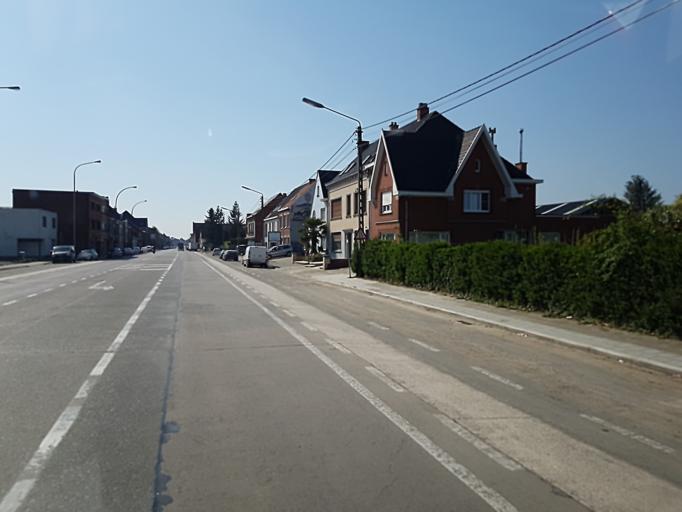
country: BE
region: Flanders
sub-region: Provincie West-Vlaanderen
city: Menen
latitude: 50.8129
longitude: 3.1210
